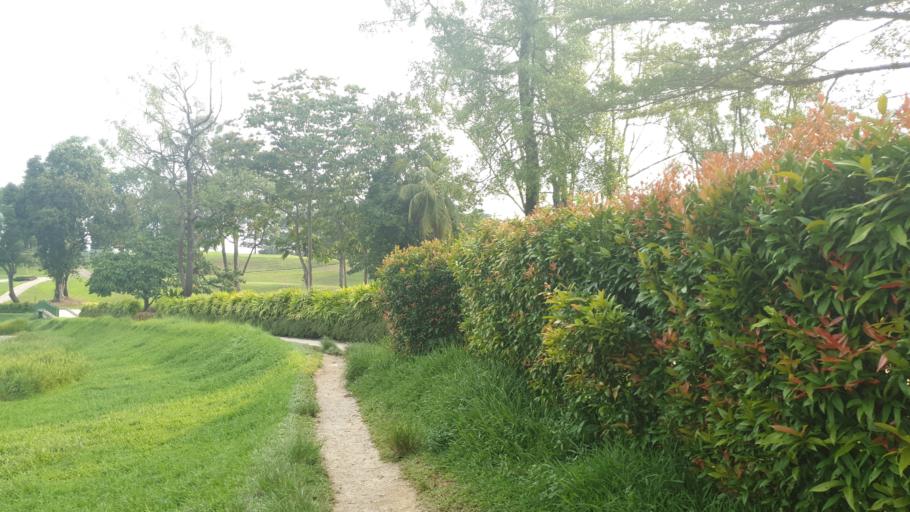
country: SG
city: Singapore
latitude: 1.3455
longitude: 103.8130
